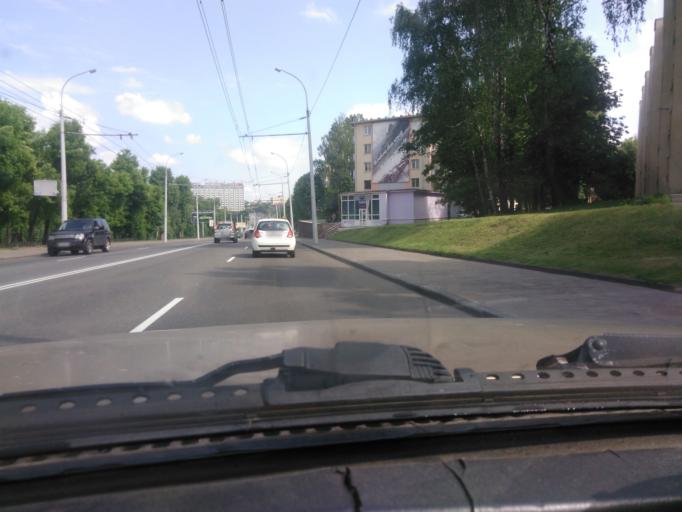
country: BY
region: Mogilev
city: Mahilyow
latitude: 53.9119
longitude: 30.3227
